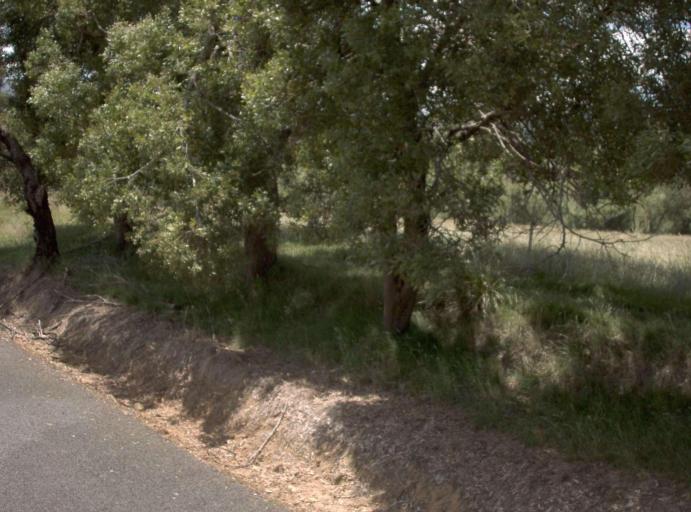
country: AU
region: New South Wales
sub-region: Bombala
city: Bombala
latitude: -37.4138
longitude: 149.0098
